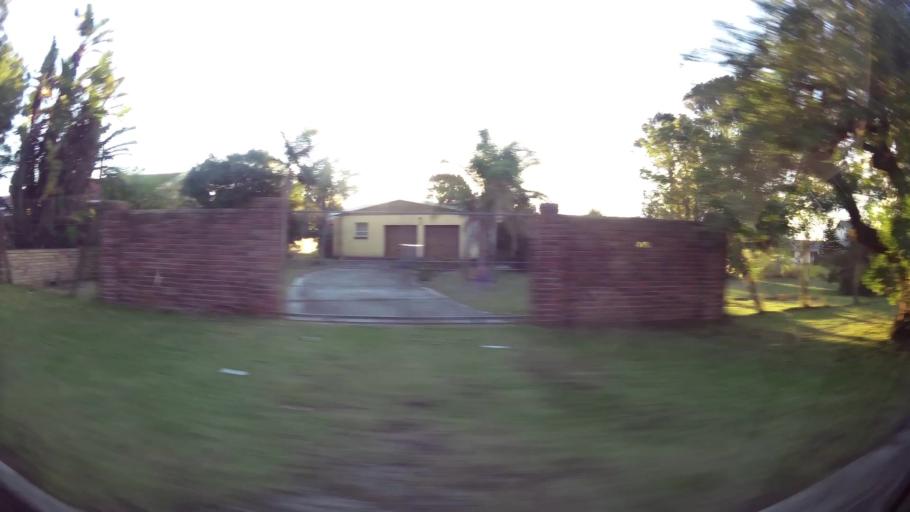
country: ZA
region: Eastern Cape
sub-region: Nelson Mandela Bay Metropolitan Municipality
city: Port Elizabeth
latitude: -33.9757
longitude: 25.5264
